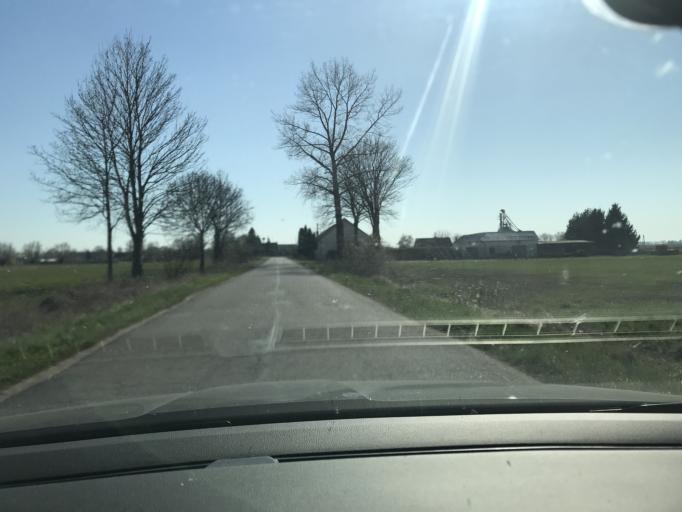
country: PL
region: Pomeranian Voivodeship
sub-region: Powiat nowodworski
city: Sztutowo
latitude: 54.3071
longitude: 19.1523
